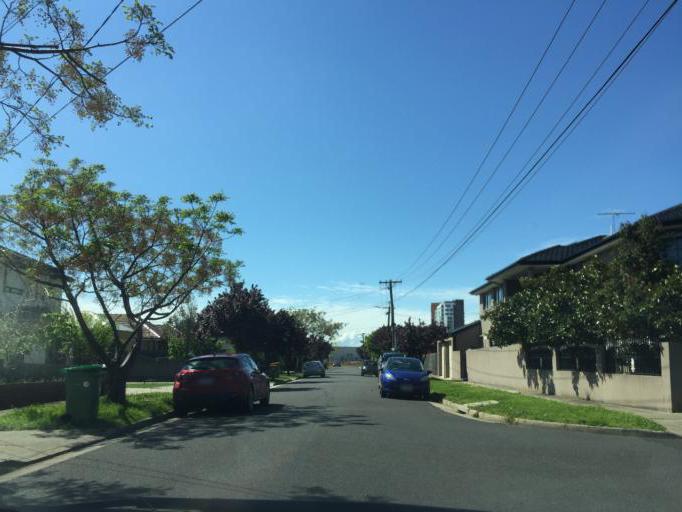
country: AU
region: Victoria
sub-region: Maribyrnong
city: Maribyrnong
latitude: -37.7790
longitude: 144.8802
